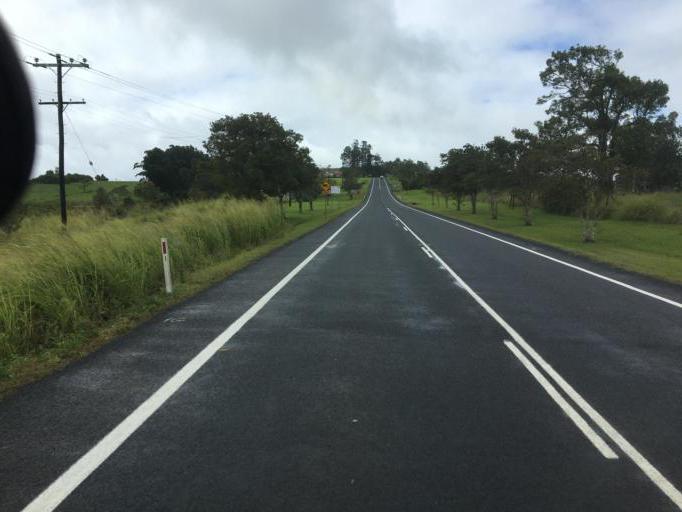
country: AU
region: Queensland
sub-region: Tablelands
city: Ravenshoe
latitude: -17.5092
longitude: 145.6176
